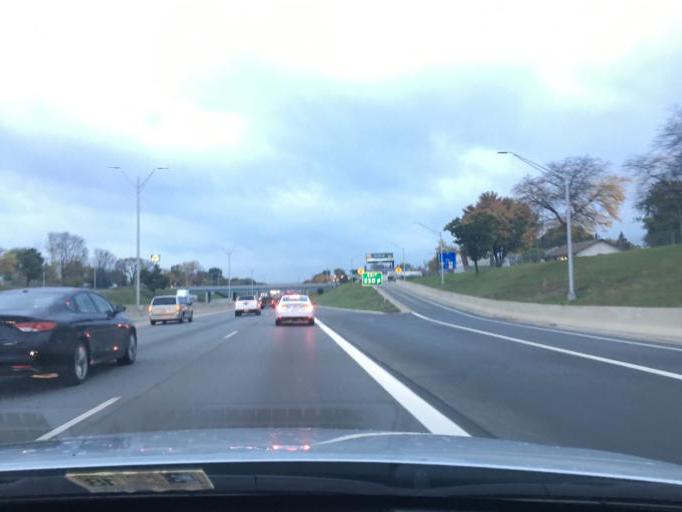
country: US
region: Michigan
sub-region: Macomb County
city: Roseville
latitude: 42.5132
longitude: -82.9186
